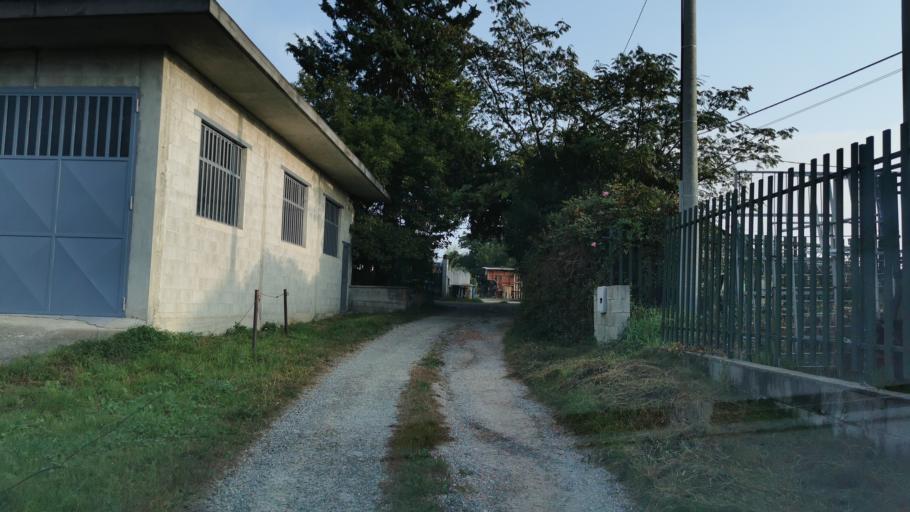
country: IT
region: Piedmont
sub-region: Provincia di Torino
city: Front
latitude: 45.2555
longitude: 7.6680
